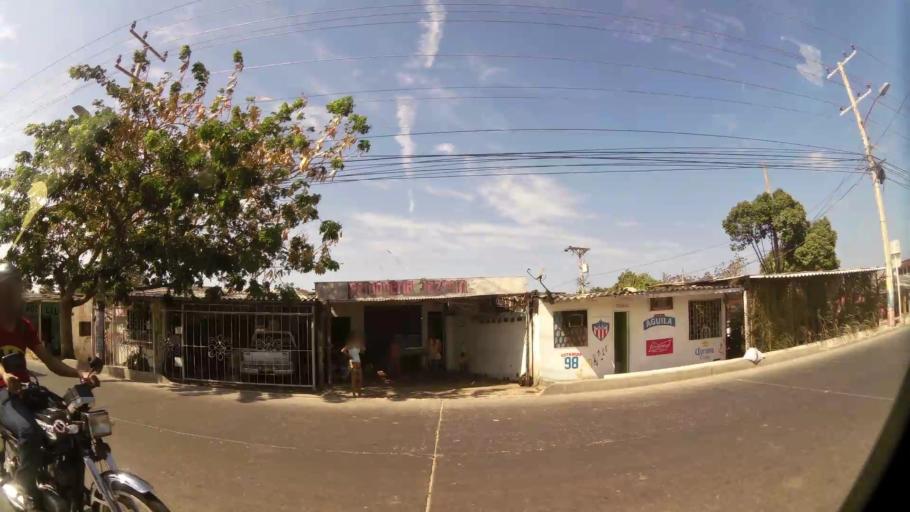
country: CO
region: Atlantico
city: Barranquilla
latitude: 10.9440
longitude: -74.8277
